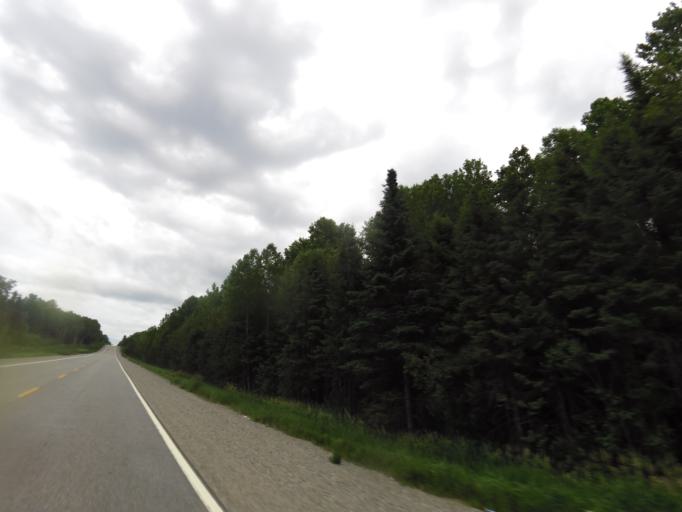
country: CA
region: Quebec
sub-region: Abitibi-Temiscamingue
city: Amos
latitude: 49.0094
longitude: -77.9620
